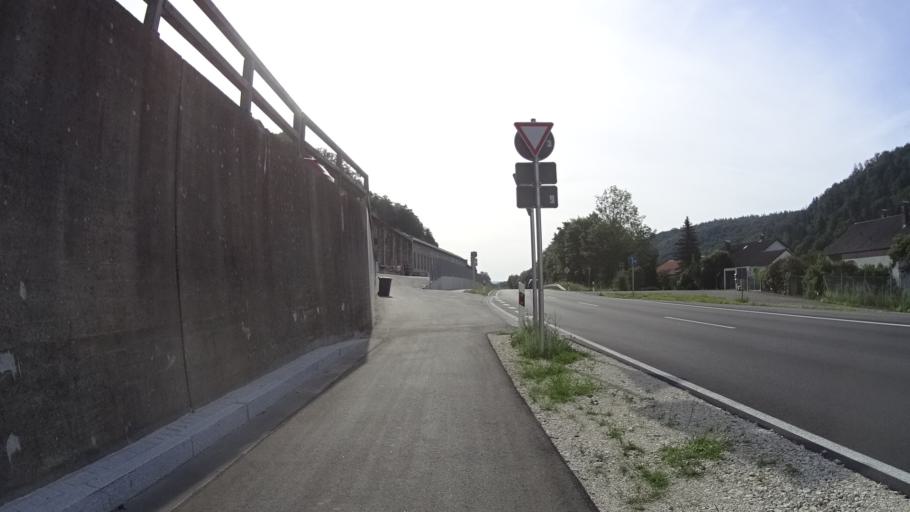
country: DE
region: Bavaria
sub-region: Lower Bavaria
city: Ihrlerstein
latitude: 48.9268
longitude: 11.8287
